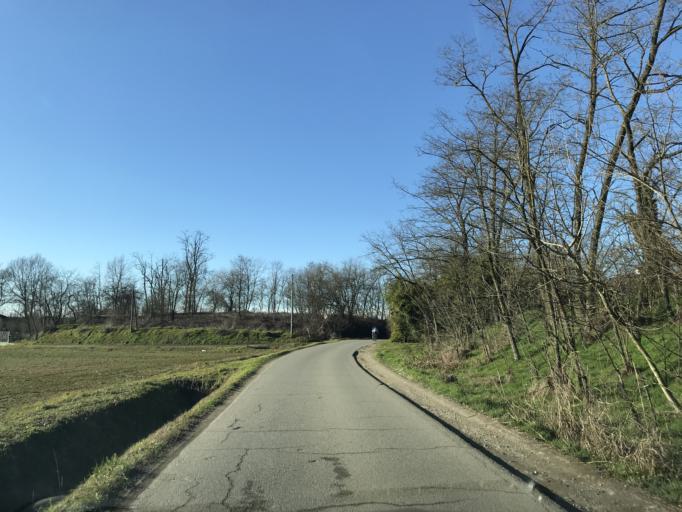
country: IT
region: Lombardy
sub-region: Provincia di Lodi
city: Bargano
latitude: 45.2341
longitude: 9.4526
